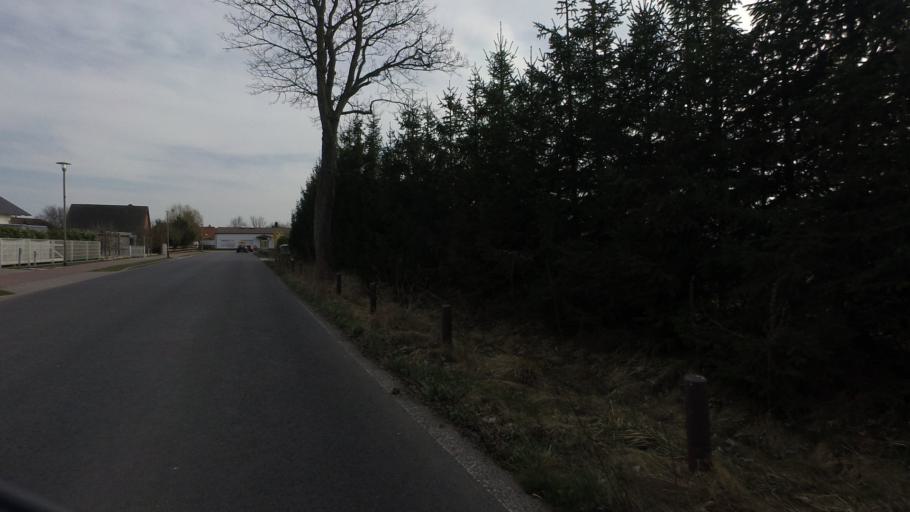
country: DE
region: Brandenburg
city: Stahnsdorf
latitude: 52.3421
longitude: 13.1996
